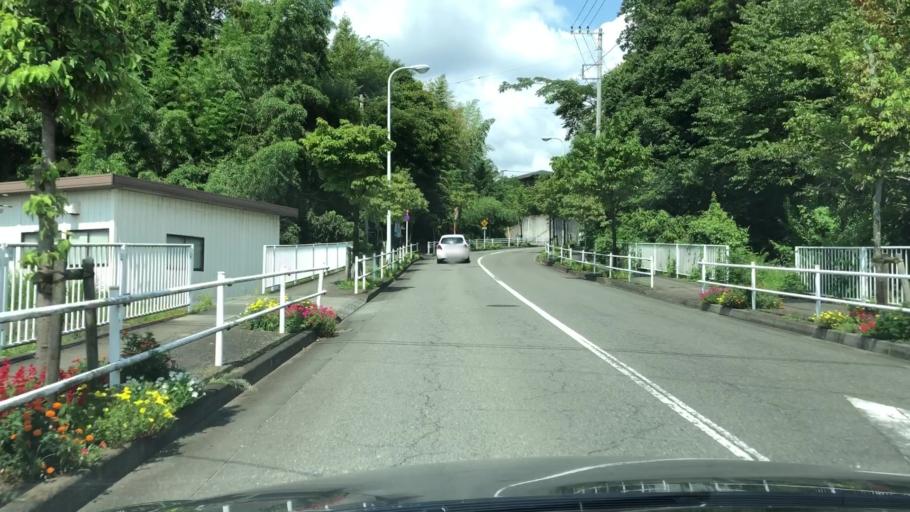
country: JP
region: Tokyo
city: Fussa
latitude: 35.7220
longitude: 139.2773
